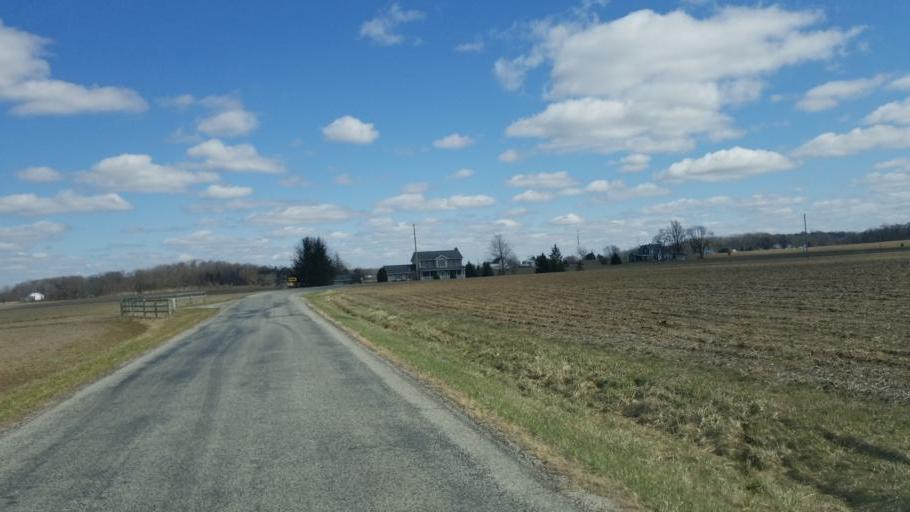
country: US
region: Ohio
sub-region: Richland County
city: Shelby
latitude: 40.8866
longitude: -82.6070
